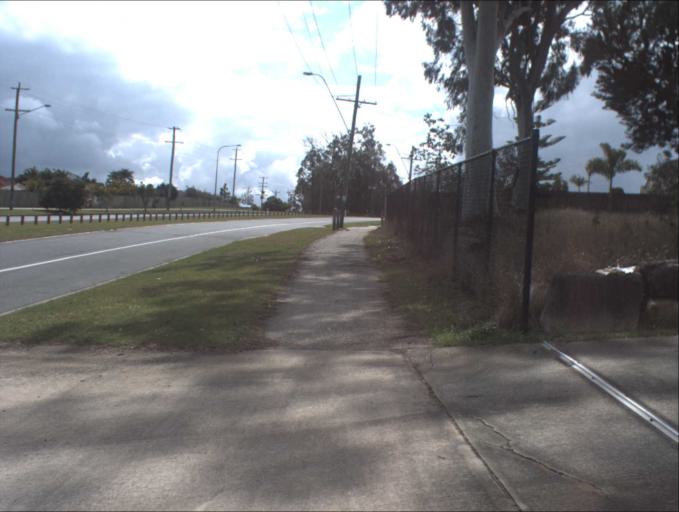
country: AU
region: Queensland
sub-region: Logan
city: Park Ridge South
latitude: -27.6841
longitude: 153.0589
